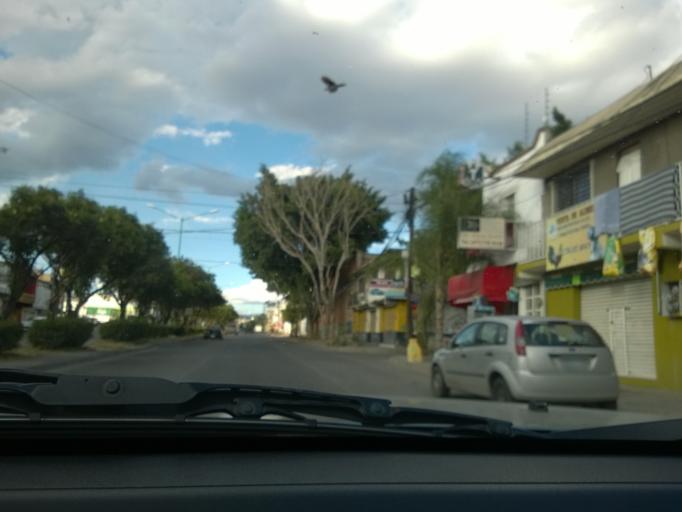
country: MX
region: Guanajuato
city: Leon
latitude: 21.1076
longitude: -101.6776
